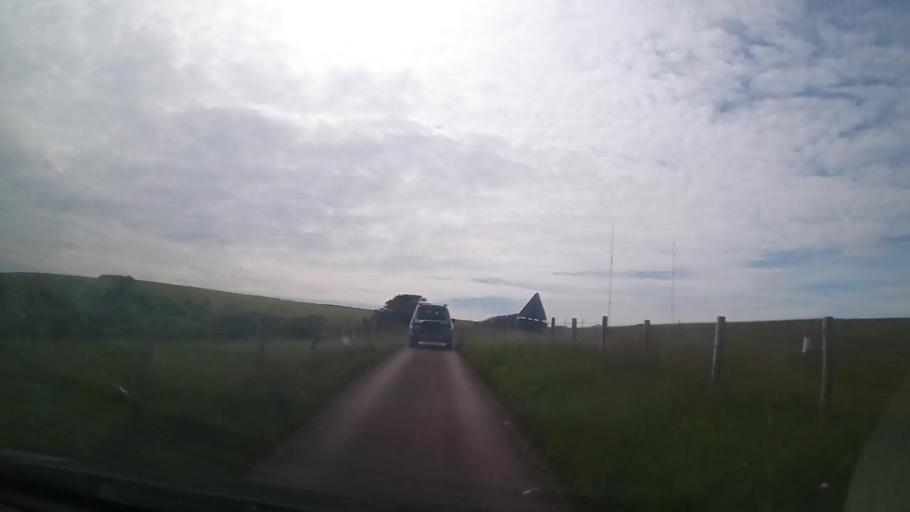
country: GB
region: England
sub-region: Devon
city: Salcombe
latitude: 50.2259
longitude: -3.6553
